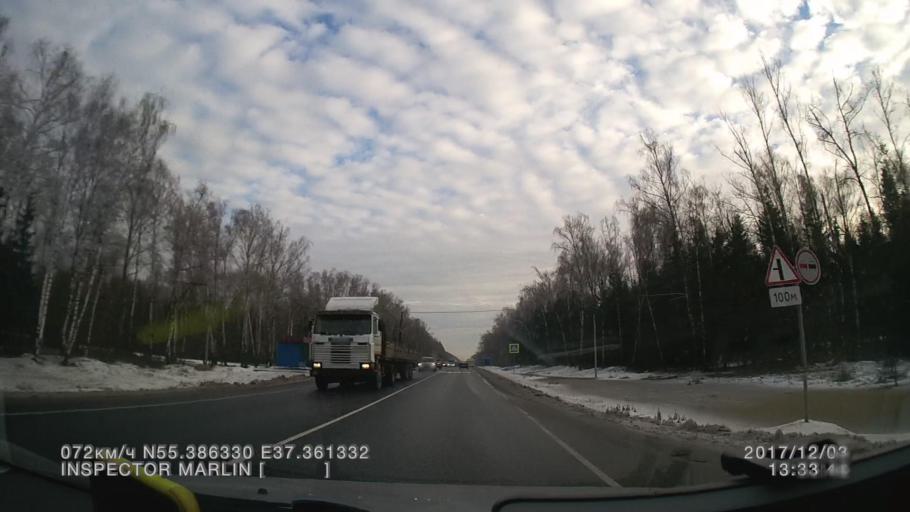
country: RU
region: Moskovskaya
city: Troitsk
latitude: 55.3863
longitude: 37.3614
